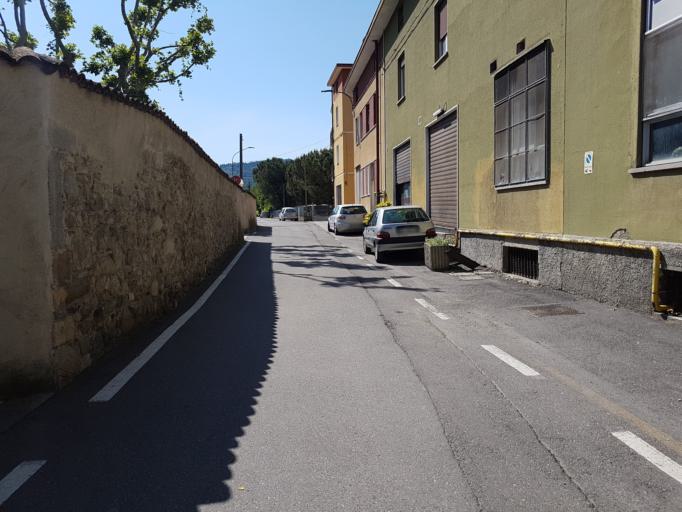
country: IT
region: Lombardy
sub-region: Provincia di Lecco
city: Calolziocorte
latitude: 45.7907
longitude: 9.4313
